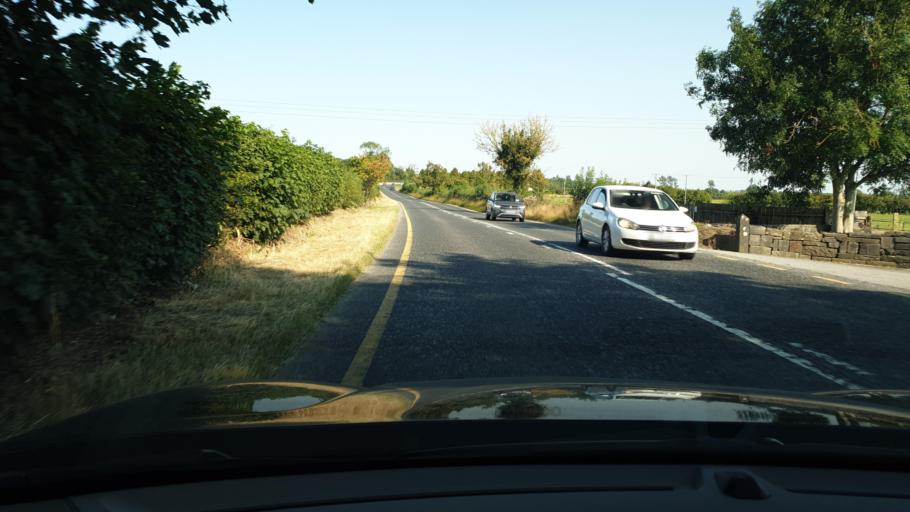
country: IE
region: Leinster
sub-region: An Mhi
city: Navan
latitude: 53.6434
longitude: -6.6286
